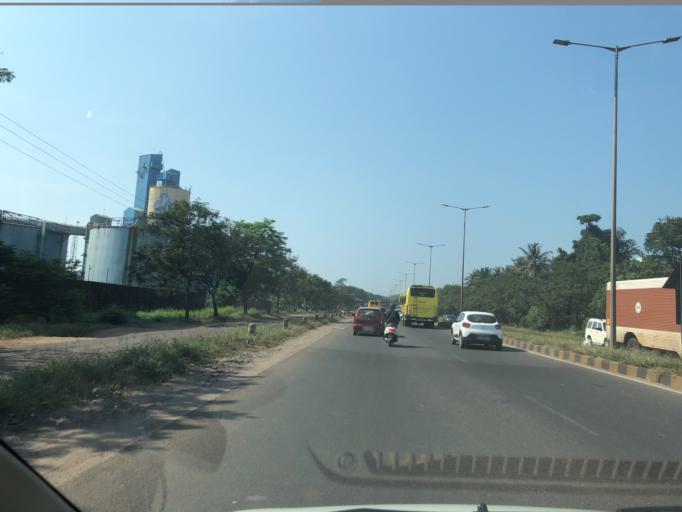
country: IN
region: Karnataka
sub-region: Dakshina Kannada
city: Mangalore
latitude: 12.9376
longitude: 74.8181
